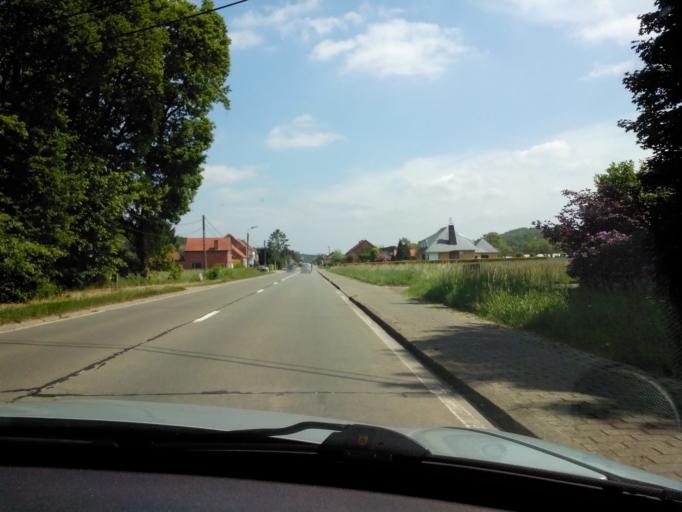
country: BE
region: Flanders
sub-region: Provincie Vlaams-Brabant
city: Holsbeek
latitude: 50.9566
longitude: 4.7672
